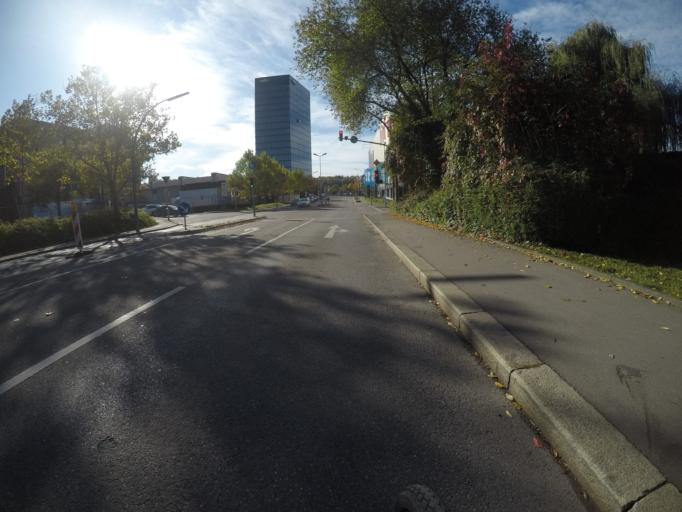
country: DE
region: Baden-Wuerttemberg
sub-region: Regierungsbezirk Stuttgart
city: Sindelfingen
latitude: 48.7045
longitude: 9.0264
